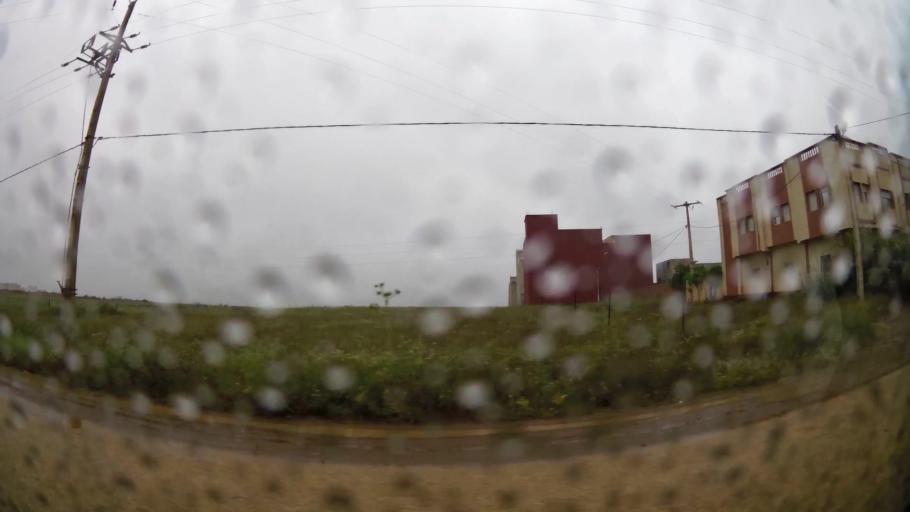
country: MA
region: Oriental
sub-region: Nador
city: Boudinar
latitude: 35.1223
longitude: -3.6457
